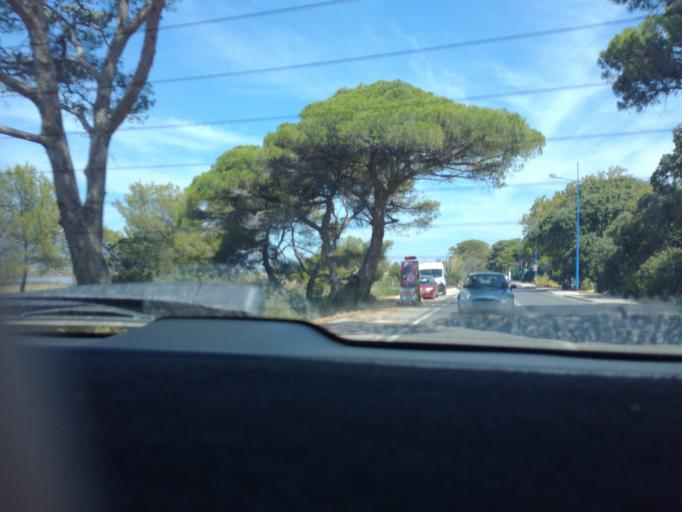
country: FR
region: Provence-Alpes-Cote d'Azur
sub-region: Departement du Var
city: Hyeres
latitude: 43.0590
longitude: 6.1470
